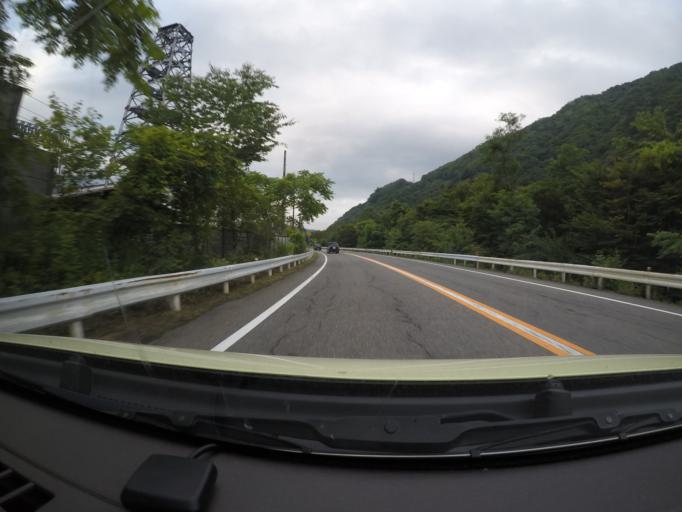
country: JP
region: Tochigi
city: Nikko
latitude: 36.7350
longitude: 139.5619
